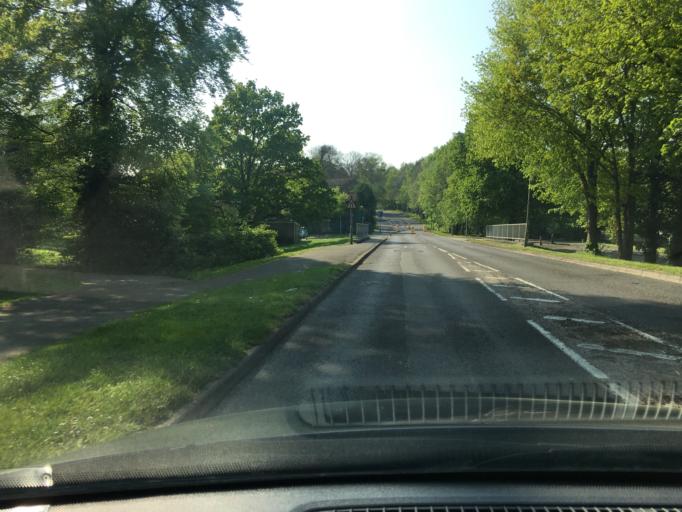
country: GB
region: England
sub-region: Bracknell Forest
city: Bracknell
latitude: 51.3952
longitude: -0.7547
